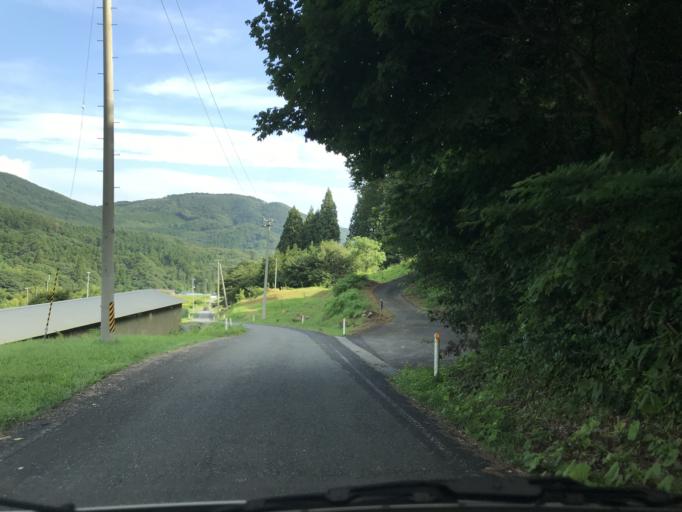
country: JP
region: Iwate
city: Ofunato
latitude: 38.9670
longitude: 141.4705
